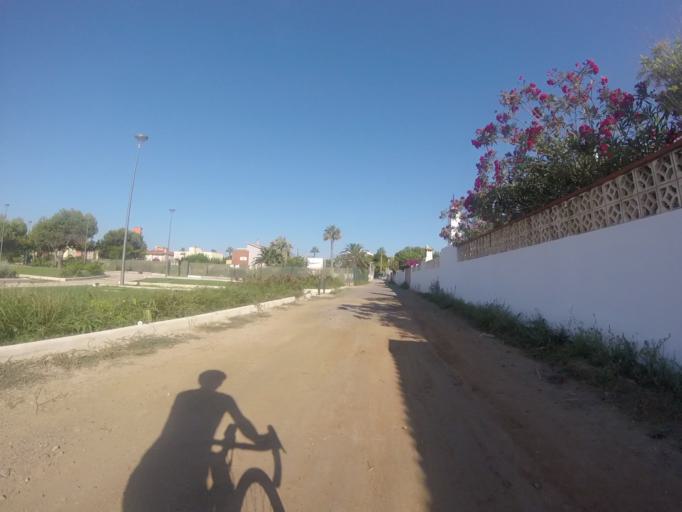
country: ES
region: Valencia
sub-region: Provincia de Castello
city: Benicarlo
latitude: 40.4047
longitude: 0.4217
